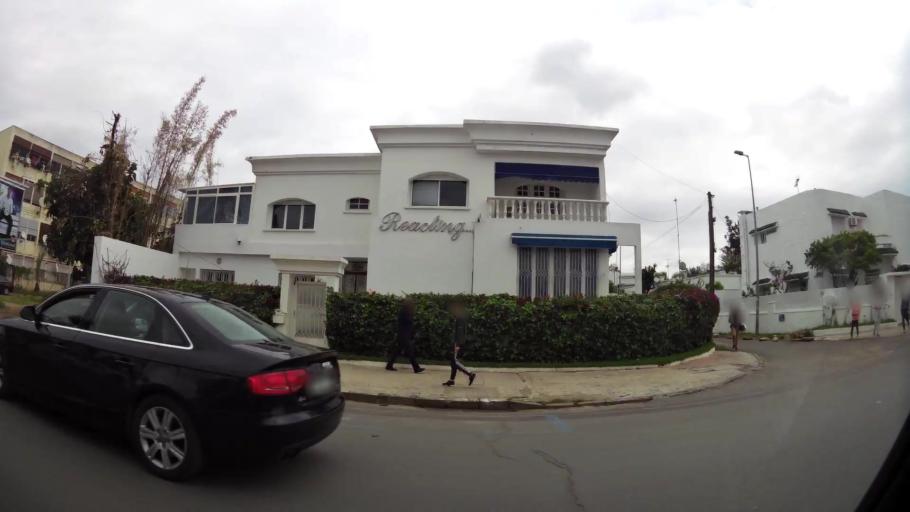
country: MA
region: Grand Casablanca
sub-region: Casablanca
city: Casablanca
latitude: 33.5751
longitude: -7.6560
